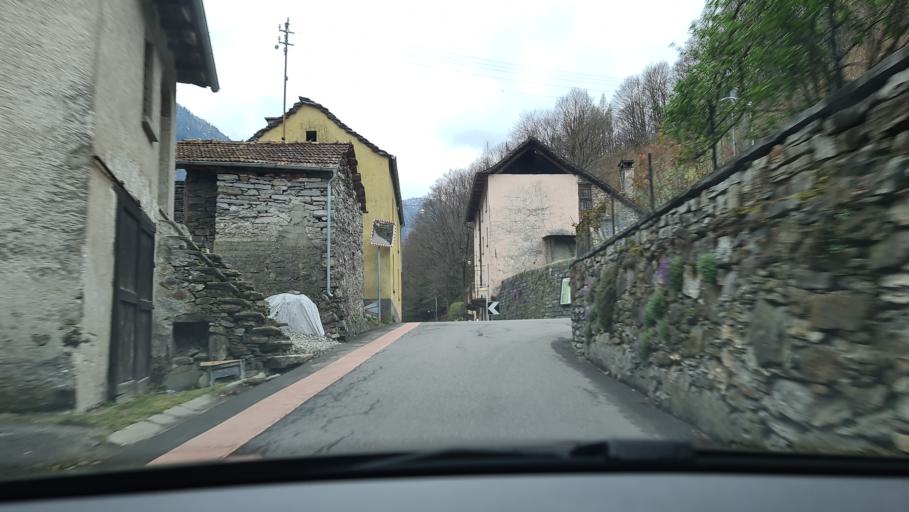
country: CH
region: Ticino
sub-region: Vallemaggia District
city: Cevio
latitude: 46.3772
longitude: 8.6602
